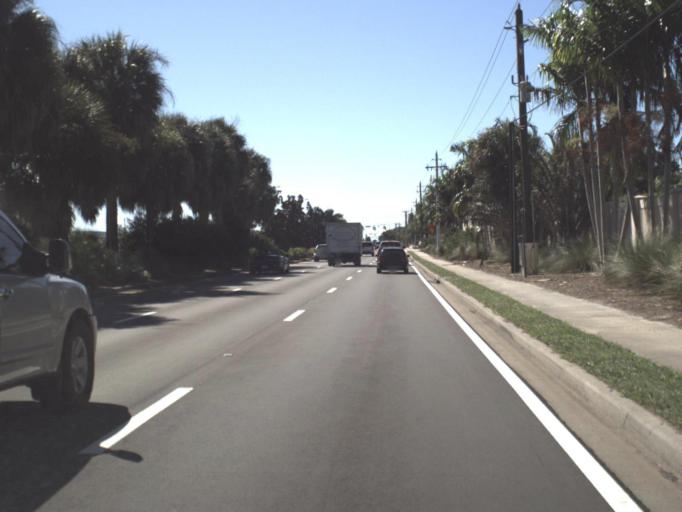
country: US
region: Florida
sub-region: Collier County
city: Naples
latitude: 26.1701
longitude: -81.7672
